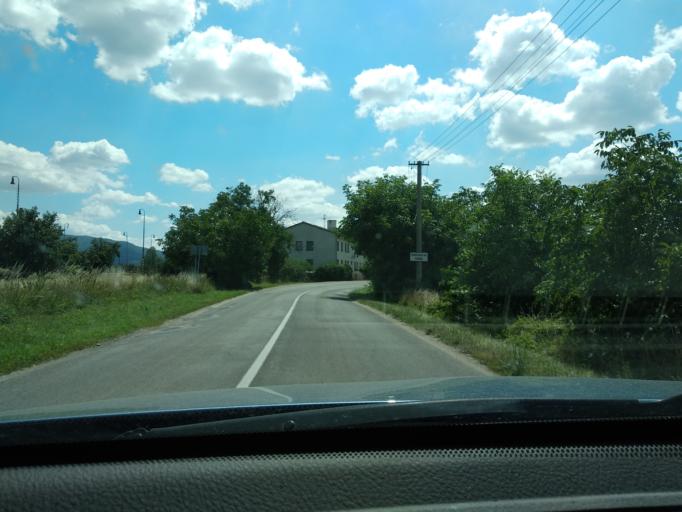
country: SK
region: Trenciansky
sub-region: Okres Trencin
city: Trencin
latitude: 48.8597
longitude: 18.0181
